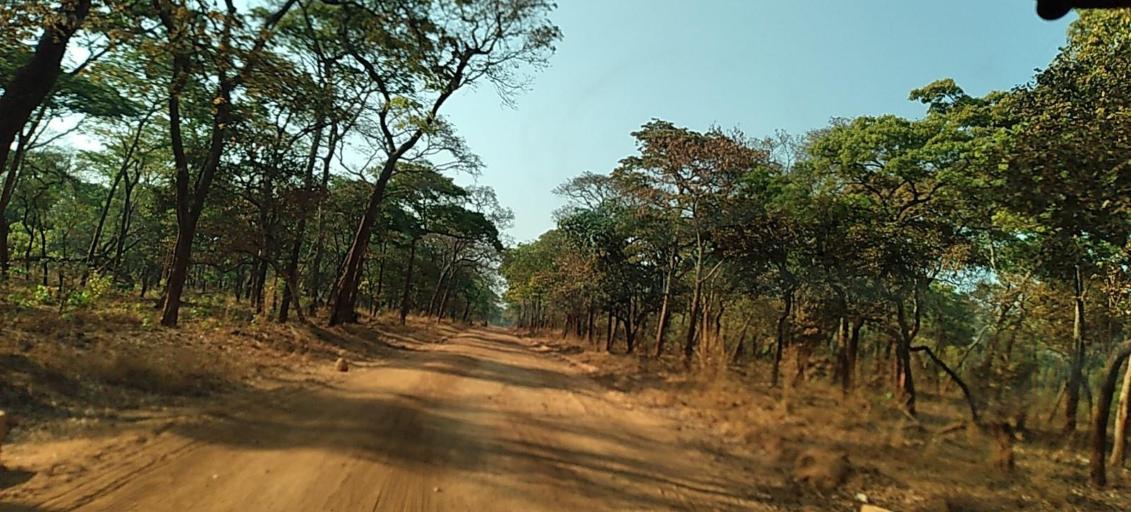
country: ZM
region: North-Western
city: Kasempa
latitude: -13.5527
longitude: 25.9975
